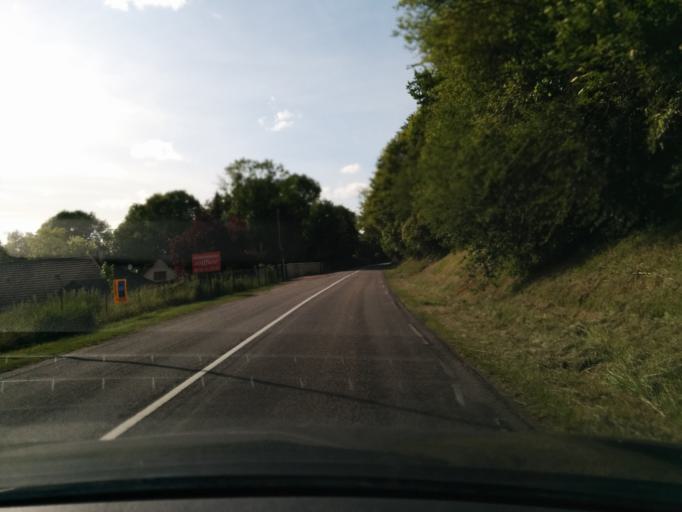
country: FR
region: Haute-Normandie
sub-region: Departement de l'Eure
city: Saint-Marcel
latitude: 49.1164
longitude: 1.4633
